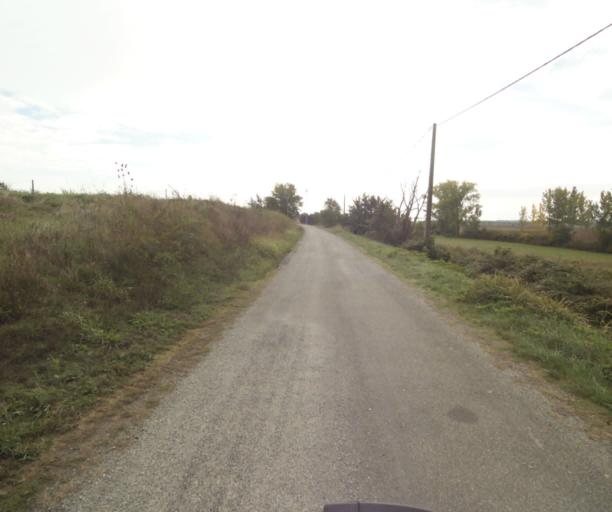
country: FR
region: Midi-Pyrenees
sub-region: Departement du Tarn-et-Garonne
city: Finhan
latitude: 43.9012
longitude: 1.2262
